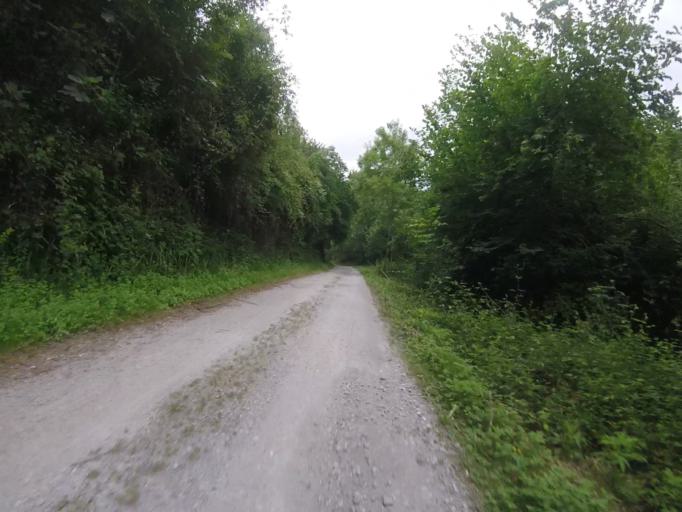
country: ES
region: Navarre
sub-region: Provincia de Navarra
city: Sunbilla
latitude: 43.1930
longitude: -1.6659
